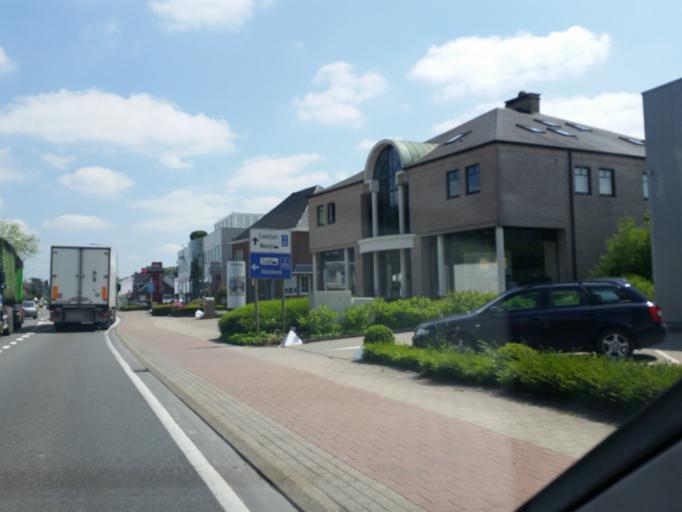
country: BE
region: Flanders
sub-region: Provincie Antwerpen
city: Rumst
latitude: 51.0414
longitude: 4.4358
